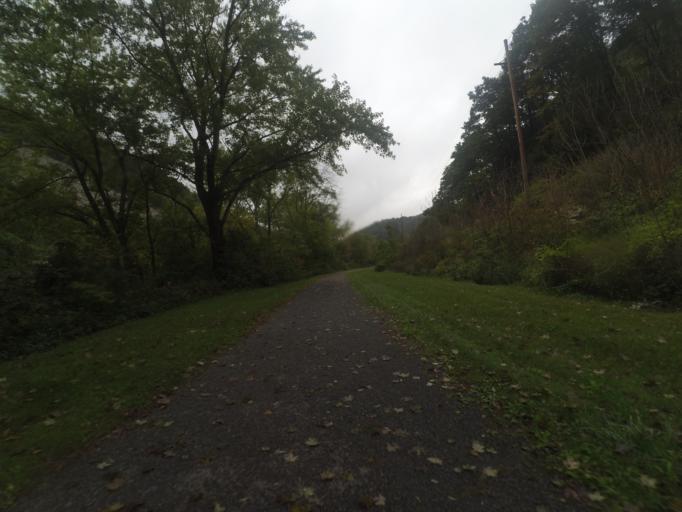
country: US
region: Pennsylvania
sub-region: Huntingdon County
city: McConnellstown
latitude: 40.5677
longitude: -78.1276
